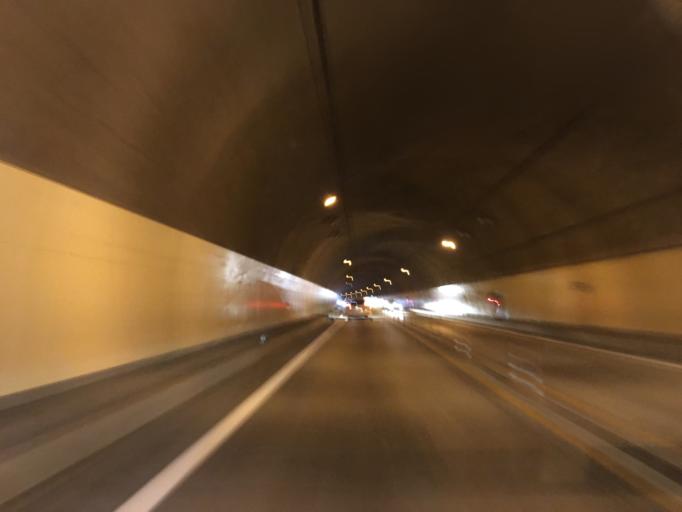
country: JP
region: Iwate
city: Kitakami
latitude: 39.2938
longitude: 141.3131
